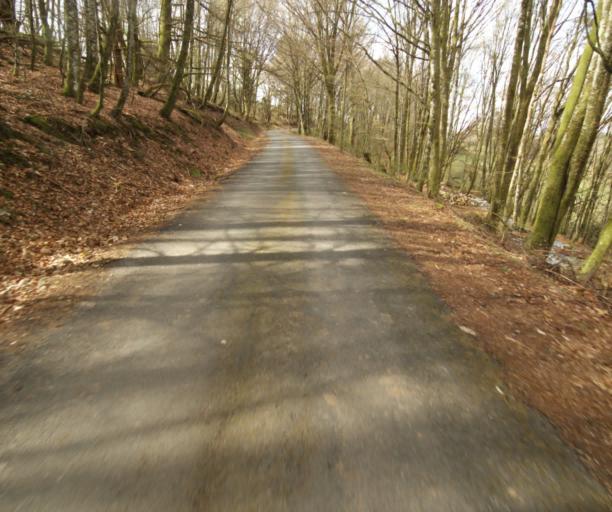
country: FR
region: Limousin
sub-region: Departement de la Correze
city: Correze
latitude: 45.3660
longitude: 1.9102
